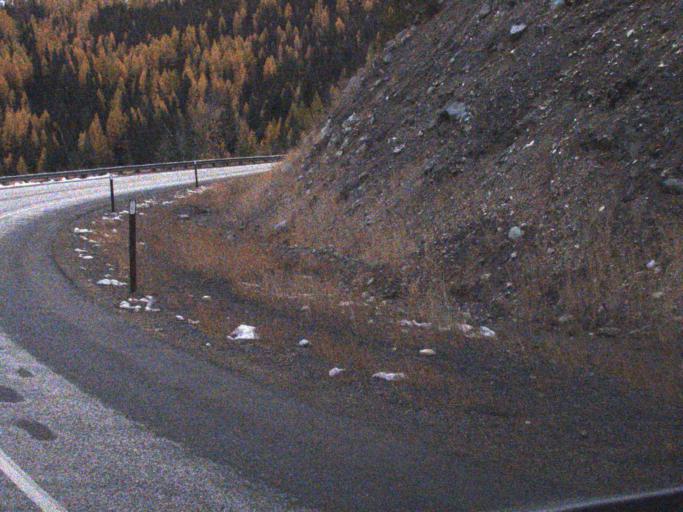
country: US
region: Washington
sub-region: Ferry County
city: Republic
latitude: 48.6048
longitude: -118.4582
